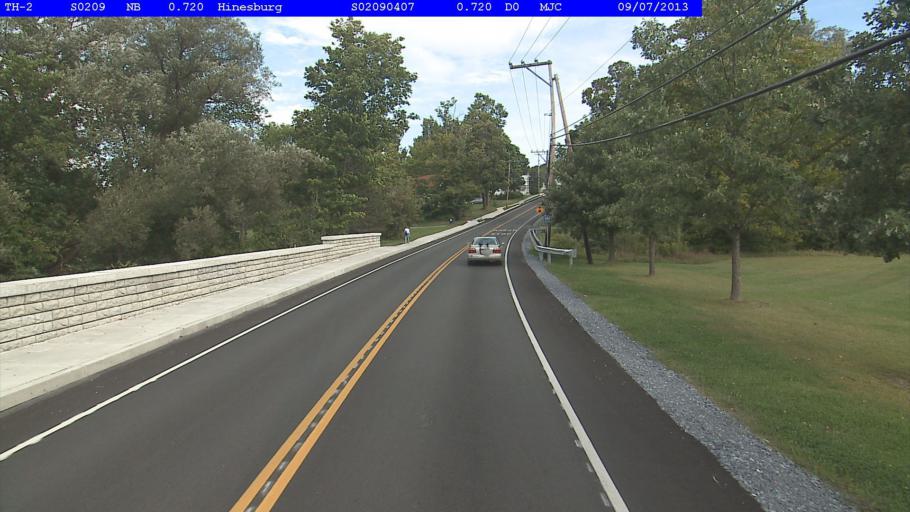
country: US
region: Vermont
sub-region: Chittenden County
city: Hinesburg
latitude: 44.3407
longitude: -73.1060
